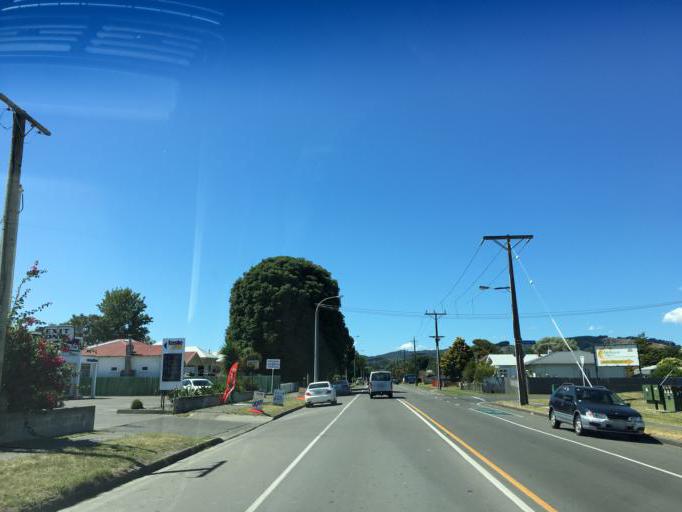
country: NZ
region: Gisborne
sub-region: Gisborne District
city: Gisborne
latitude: -38.6640
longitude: 178.0061
